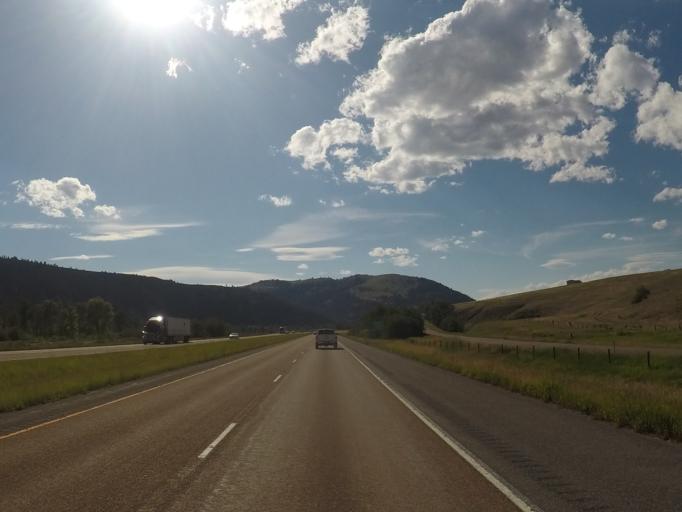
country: US
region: Montana
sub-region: Granite County
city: Philipsburg
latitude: 46.6796
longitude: -113.1829
